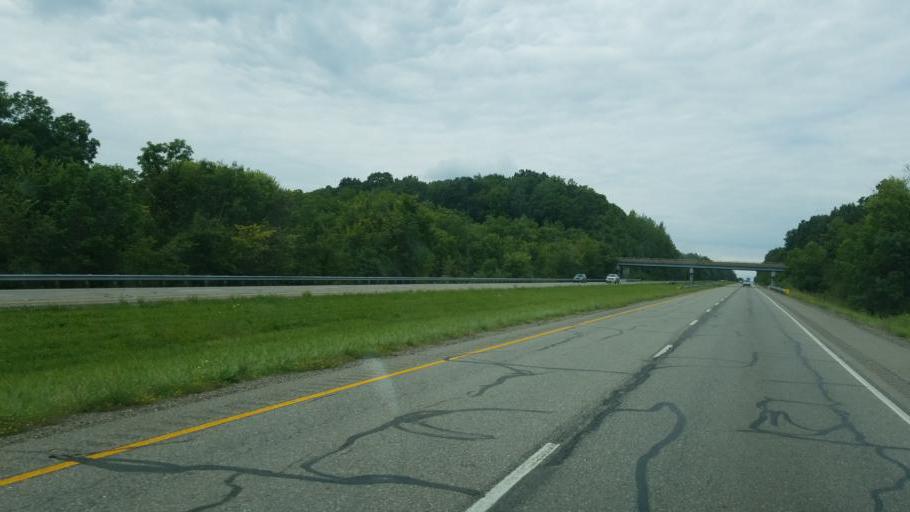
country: US
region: Ohio
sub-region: Columbiana County
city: Lisbon
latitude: 40.7834
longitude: -80.7374
